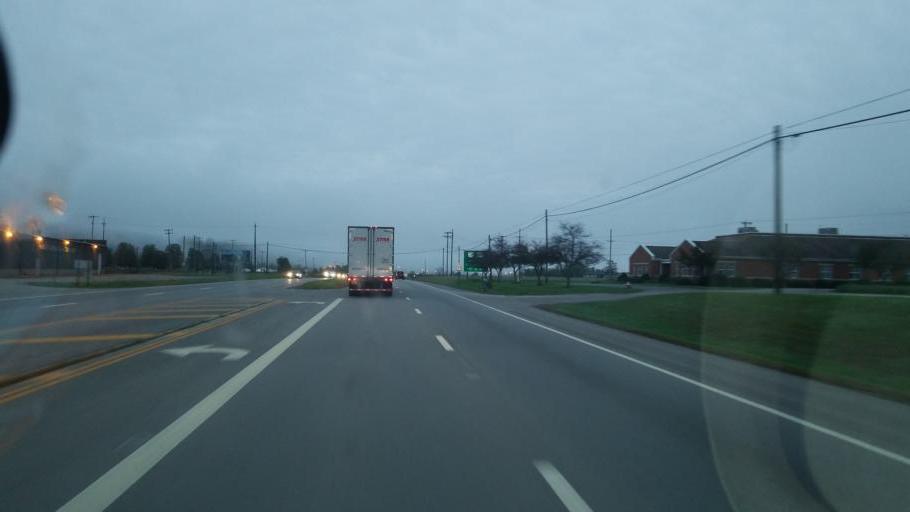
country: US
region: Ohio
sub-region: Pike County
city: Piketon
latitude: 39.0588
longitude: -83.0194
